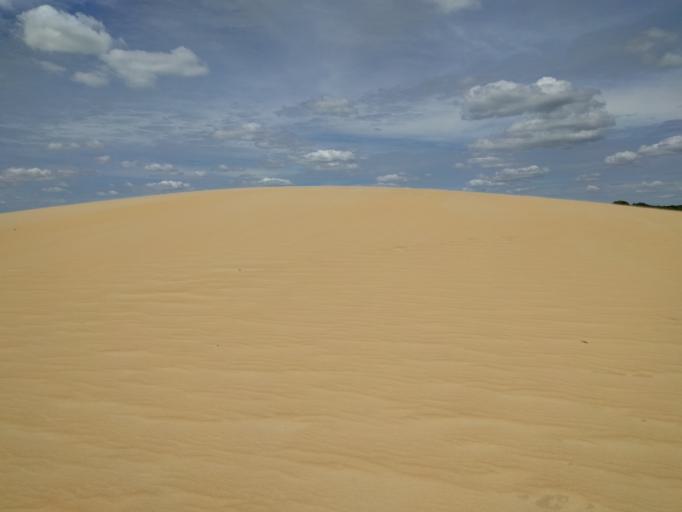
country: BO
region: Santa Cruz
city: Santa Cruz de la Sierra
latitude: -17.9483
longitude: -63.1588
